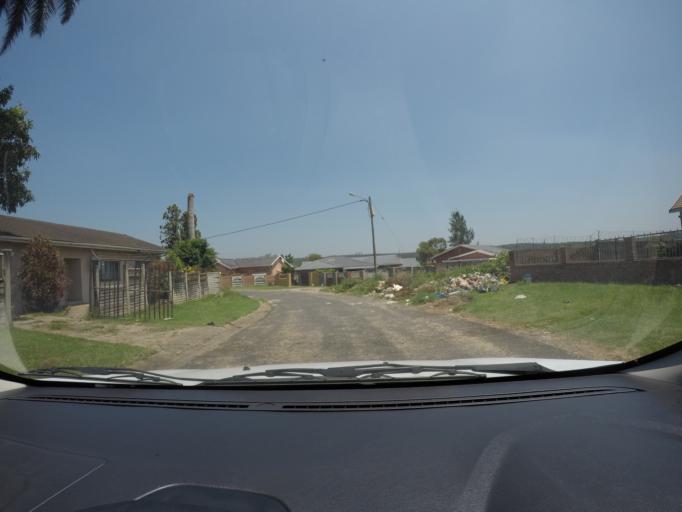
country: ZA
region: KwaZulu-Natal
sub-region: uThungulu District Municipality
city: eSikhawini
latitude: -28.8689
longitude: 31.9115
